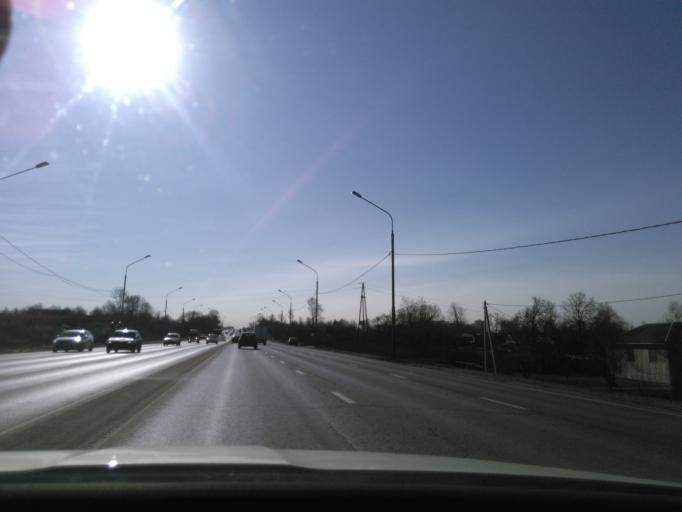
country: RU
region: Moskovskaya
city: Novopodrezkovo
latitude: 55.9304
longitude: 37.3791
